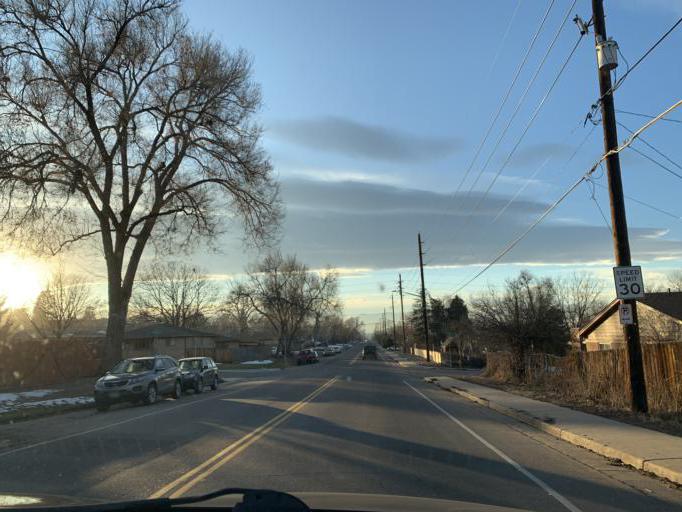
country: US
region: Colorado
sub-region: Adams County
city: Berkley
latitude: 39.7912
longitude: -105.0352
